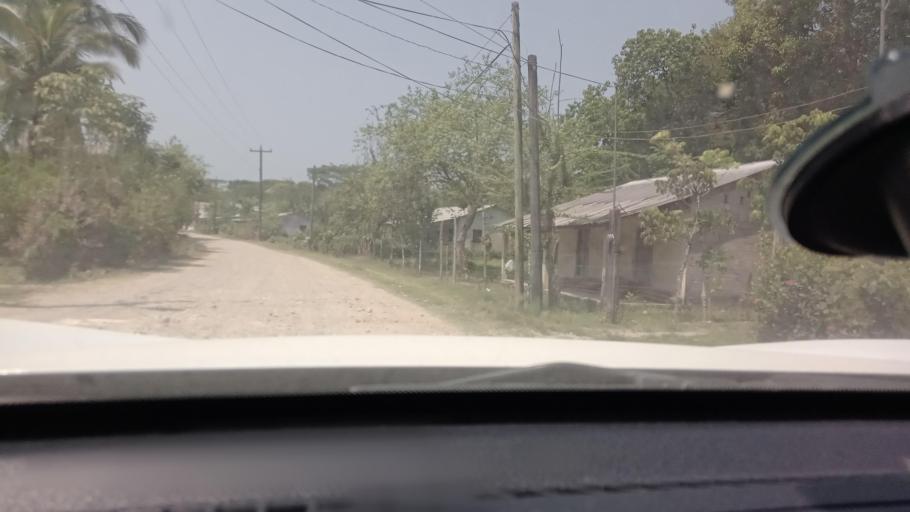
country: MX
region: Tabasco
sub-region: Huimanguillo
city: Francisco Rueda
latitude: 17.5029
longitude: -93.9033
